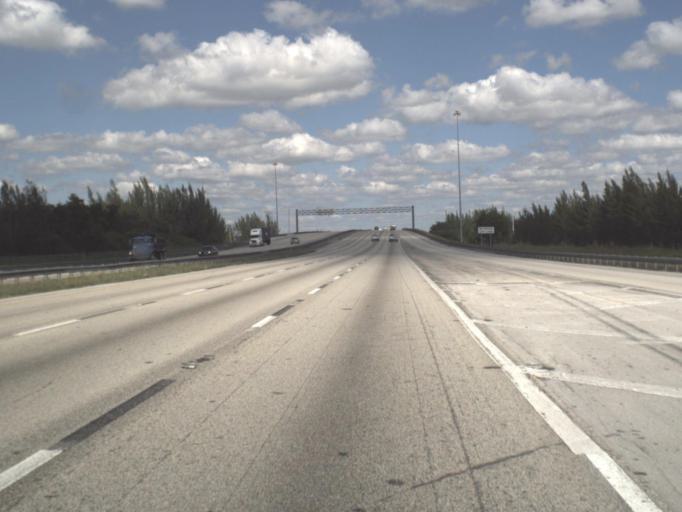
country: US
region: Florida
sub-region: Miami-Dade County
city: Doral
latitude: 25.8717
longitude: -80.3879
